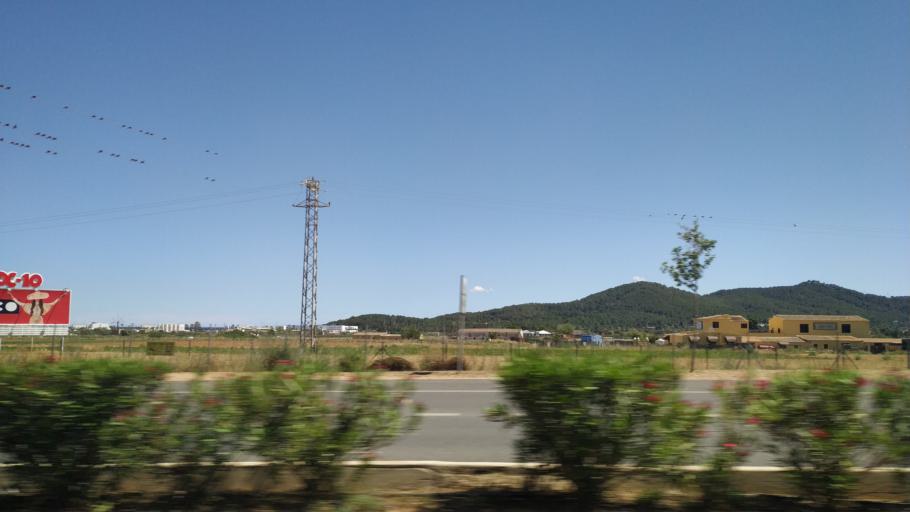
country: ES
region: Balearic Islands
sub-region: Illes Balears
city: Ibiza
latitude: 38.8840
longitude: 1.3893
